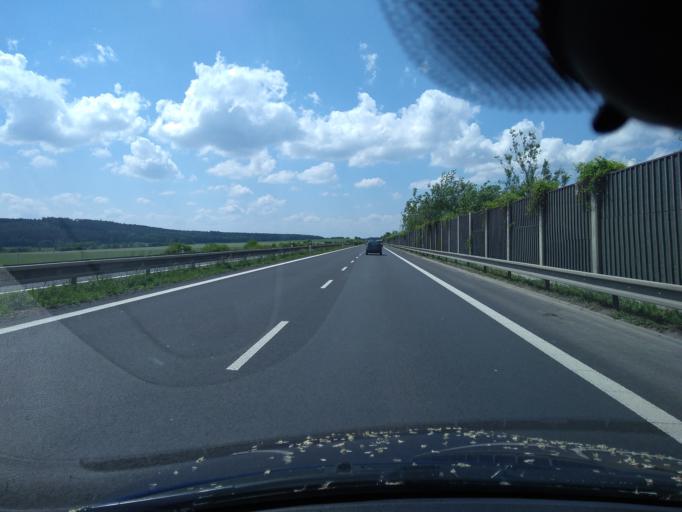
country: CZ
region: Plzensky
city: Stenovice
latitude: 49.6748
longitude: 13.3576
